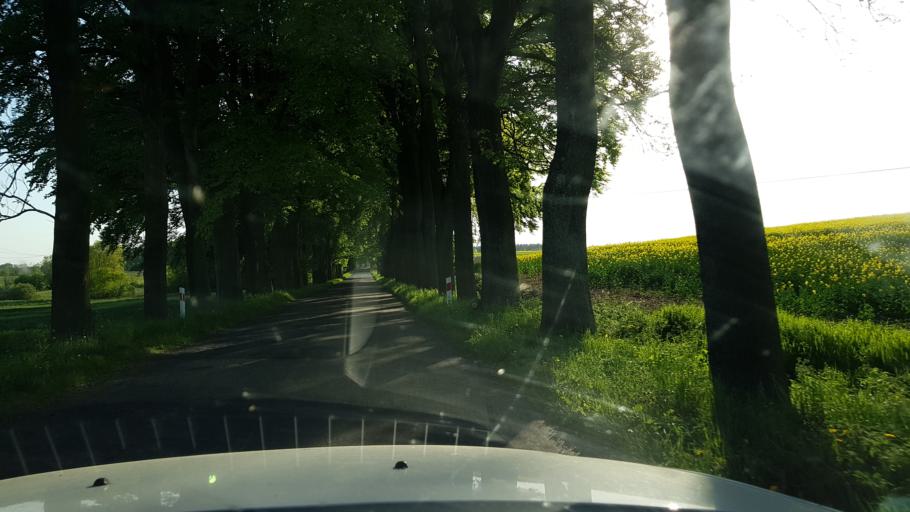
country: PL
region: West Pomeranian Voivodeship
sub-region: Powiat lobeski
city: Dobra
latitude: 53.5866
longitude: 15.2903
